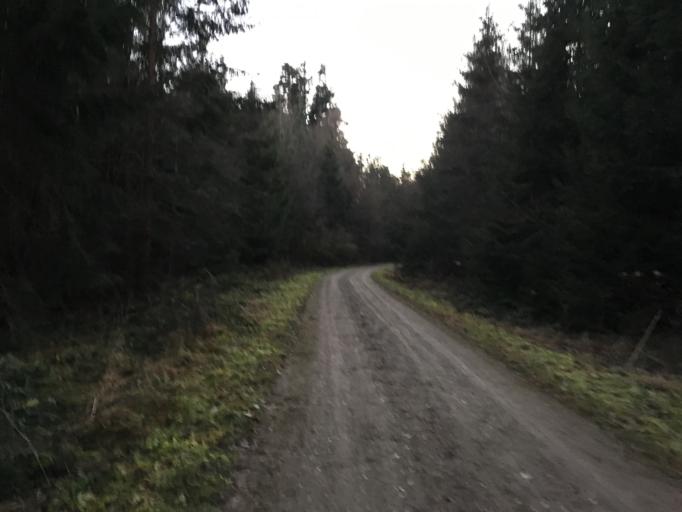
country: DE
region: Bavaria
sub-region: Swabia
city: Bohen
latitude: 47.8686
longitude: 10.2878
